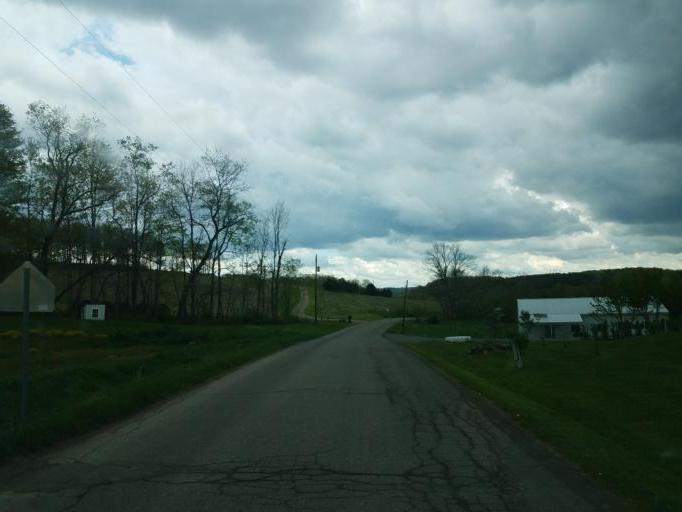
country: US
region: Ohio
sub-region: Knox County
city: Oak Hill
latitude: 40.4432
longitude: -82.2144
